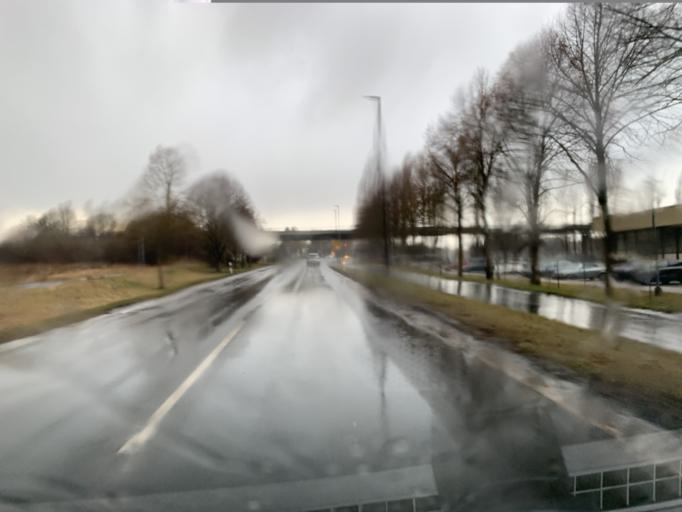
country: DE
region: Baden-Wuerttemberg
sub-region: Regierungsbezirk Stuttgart
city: Magstadt
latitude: 48.7100
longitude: 8.9824
